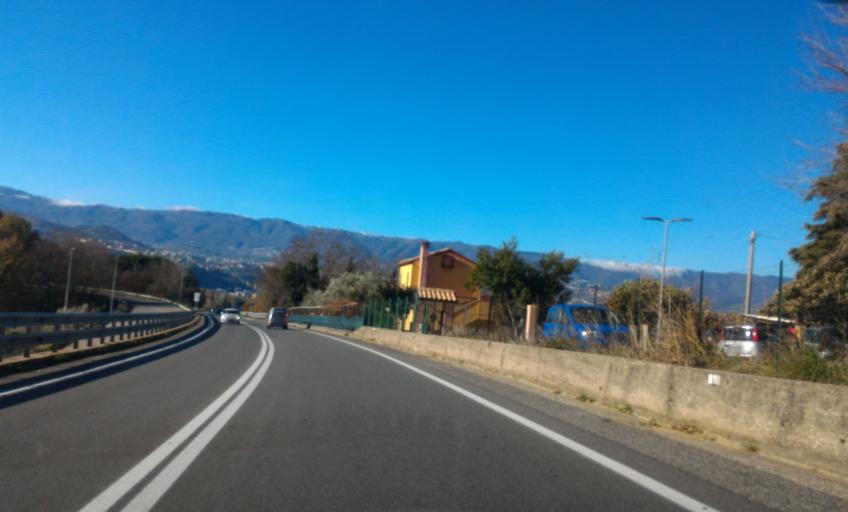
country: IT
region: Calabria
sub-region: Provincia di Cosenza
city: Zumpano
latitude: 39.2955
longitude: 16.2764
